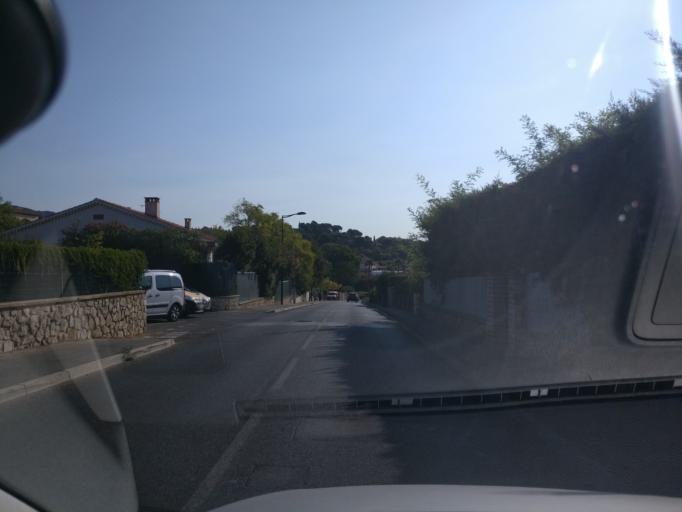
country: FR
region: Provence-Alpes-Cote d'Azur
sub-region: Departement du Var
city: Ollioules
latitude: 43.1350
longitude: 5.8448
